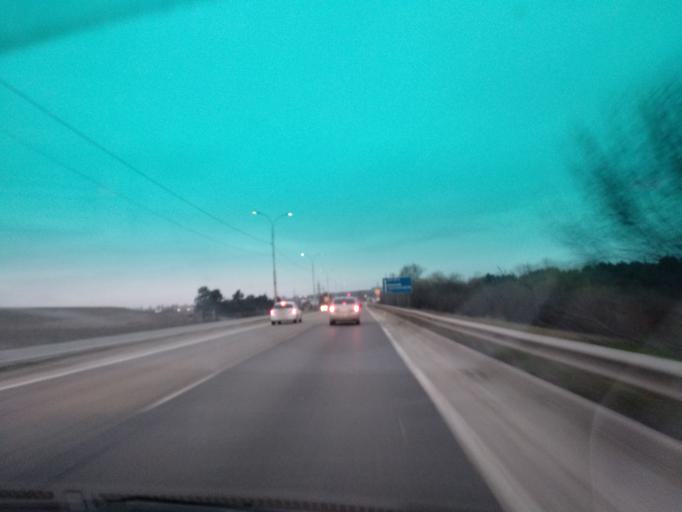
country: RU
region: Adygeya
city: Tlyustenkhabl'
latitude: 44.9838
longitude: 39.1144
